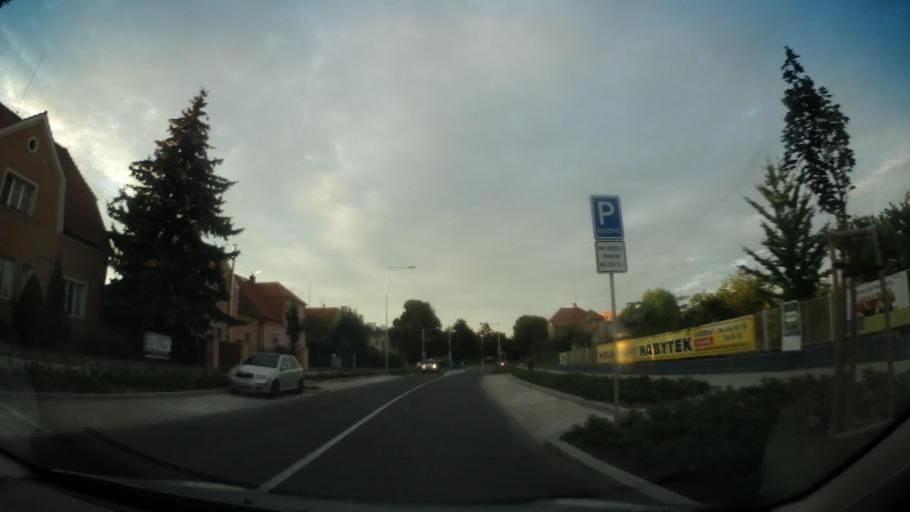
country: CZ
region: Central Bohemia
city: Lysa nad Labem
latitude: 50.2058
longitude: 14.8432
